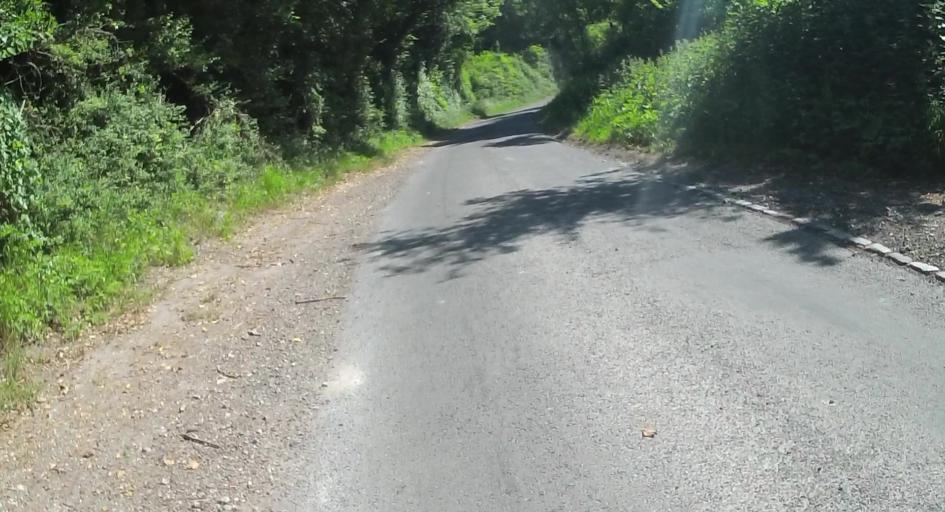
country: GB
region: England
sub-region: Hampshire
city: Kingsclere
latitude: 51.3117
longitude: -1.2947
